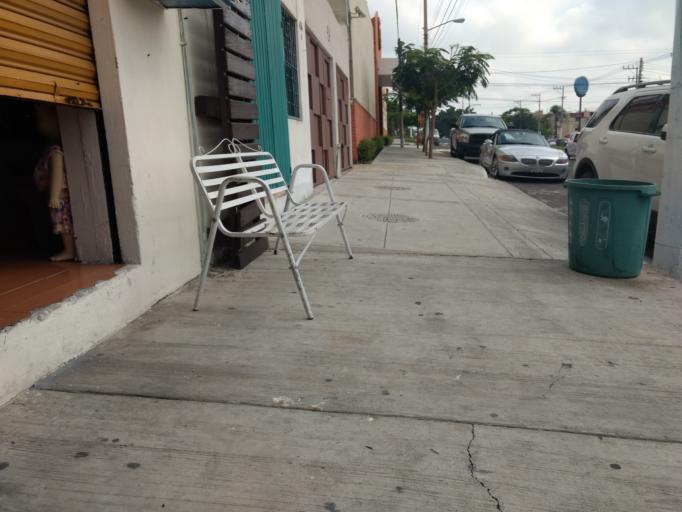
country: MX
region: Jalisco
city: Guadalajara
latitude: 20.6694
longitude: -103.4360
